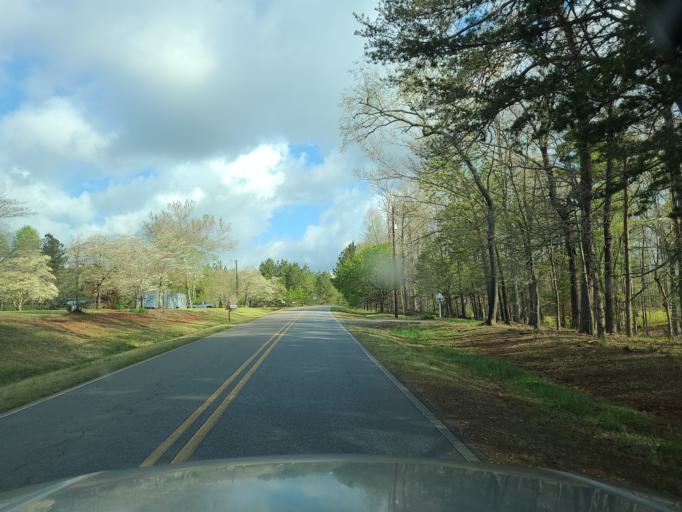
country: US
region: North Carolina
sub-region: Rutherford County
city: Forest City
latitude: 35.4374
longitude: -81.8333
